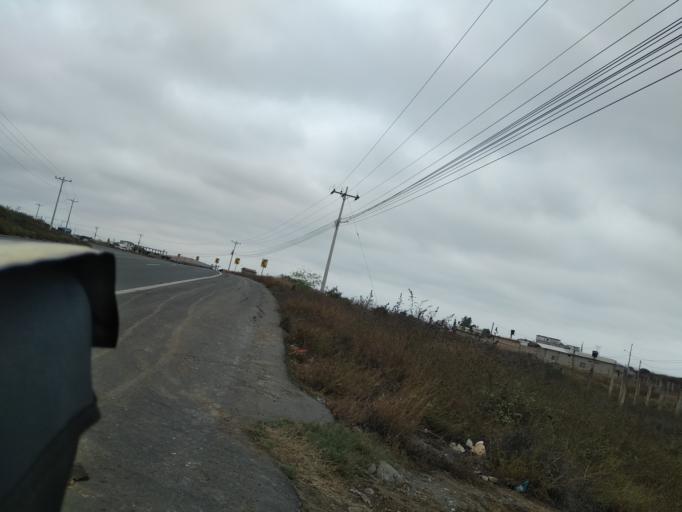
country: EC
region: Santa Elena
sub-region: Canton Santa Elena
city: Santa Elena
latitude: -2.2061
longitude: -80.8624
